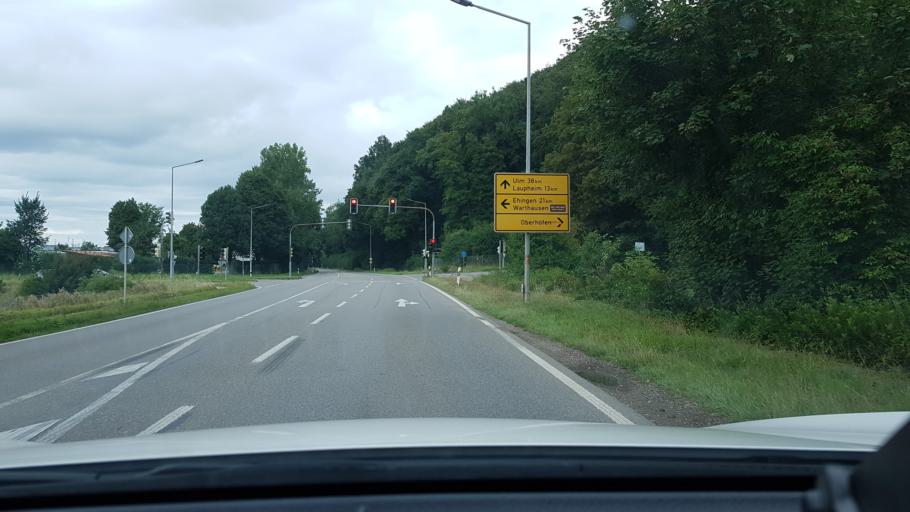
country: DE
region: Baden-Wuerttemberg
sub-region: Tuebingen Region
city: Warthausen
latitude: 48.1306
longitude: 9.8060
